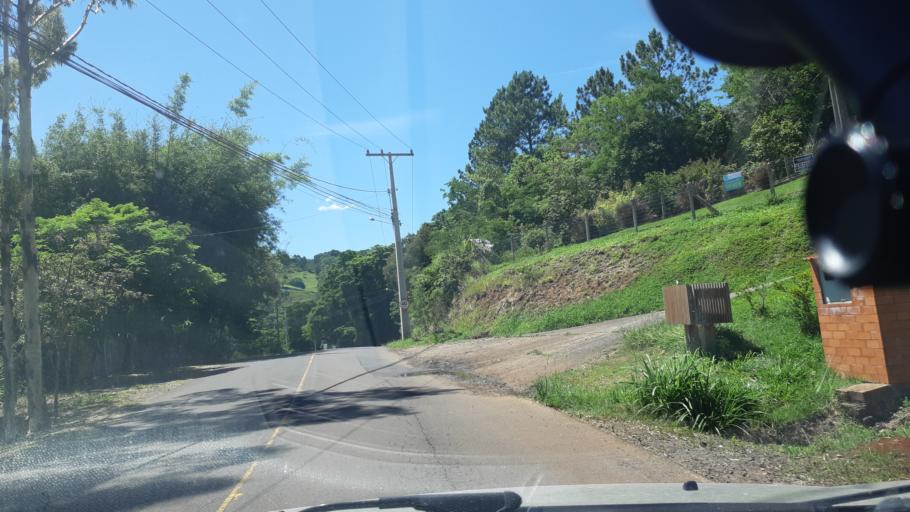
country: BR
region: Rio Grande do Sul
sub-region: Novo Hamburgo
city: Novo Hamburgo
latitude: -29.6260
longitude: -51.0998
